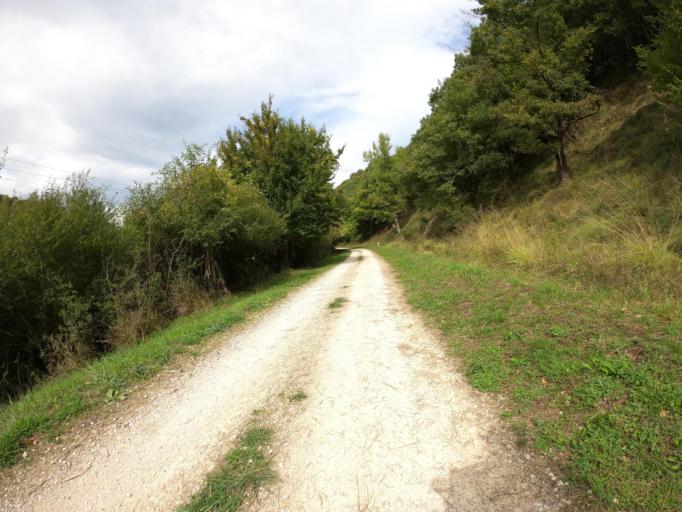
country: ES
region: Navarre
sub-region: Provincia de Navarra
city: Irurtzun
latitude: 42.9597
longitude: -1.8242
